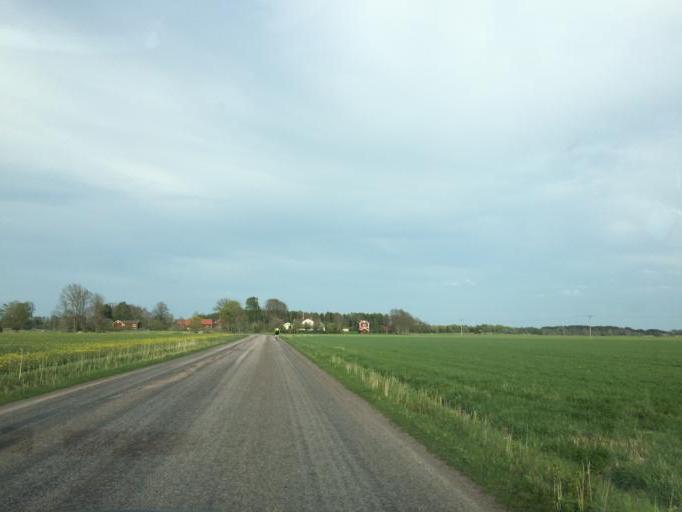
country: SE
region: Vaestmanland
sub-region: Hallstahammars Kommun
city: Hallstahammar
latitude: 59.6003
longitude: 16.1808
